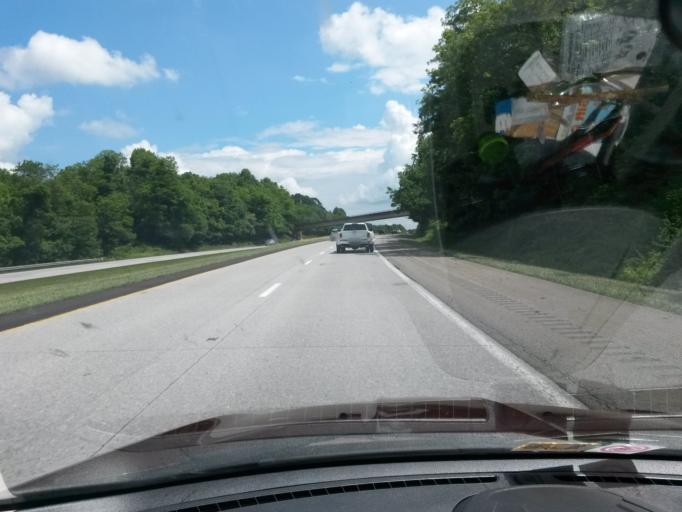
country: US
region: Virginia
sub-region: Carroll County
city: Cana
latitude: 36.5142
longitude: -80.7427
